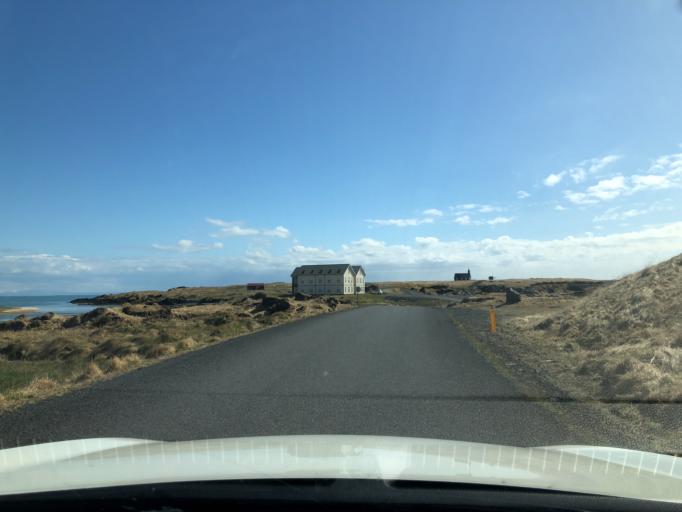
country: IS
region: West
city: Olafsvik
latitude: 64.8247
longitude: -23.3868
